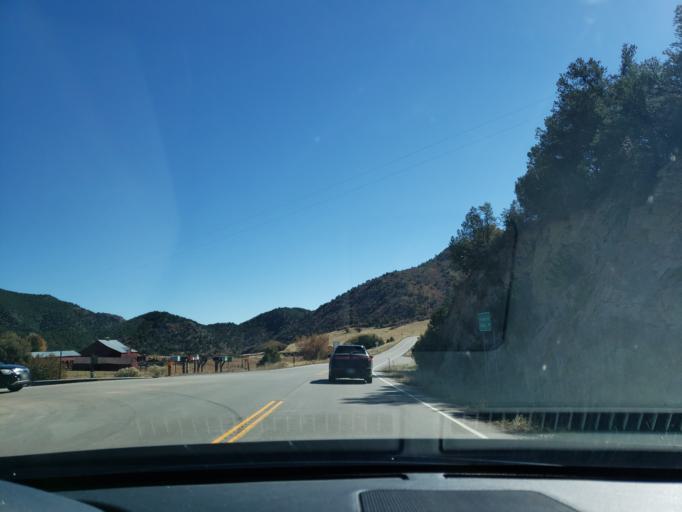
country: US
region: Colorado
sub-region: Fremont County
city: Canon City
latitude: 38.5858
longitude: -105.4184
